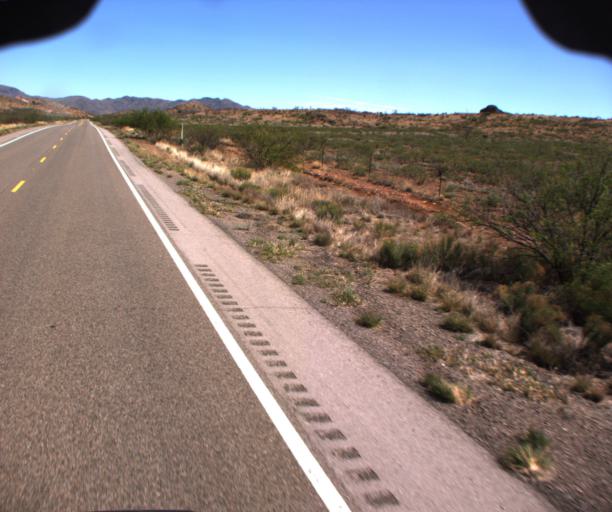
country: US
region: Arizona
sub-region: Cochise County
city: Douglas
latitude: 31.4686
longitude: -109.4521
